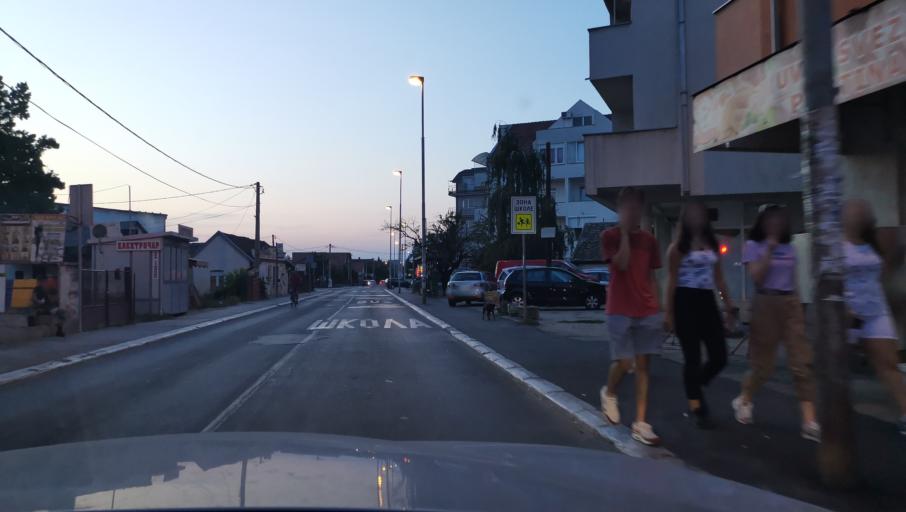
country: RS
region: Central Serbia
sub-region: Belgrade
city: Obrenovac
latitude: 44.6605
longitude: 20.2037
